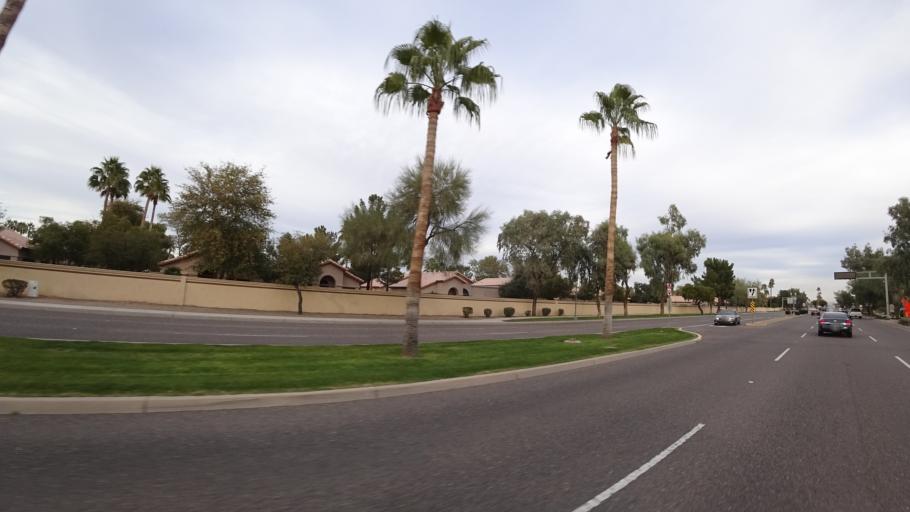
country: US
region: Arizona
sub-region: Maricopa County
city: Surprise
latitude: 33.6386
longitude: -112.3662
